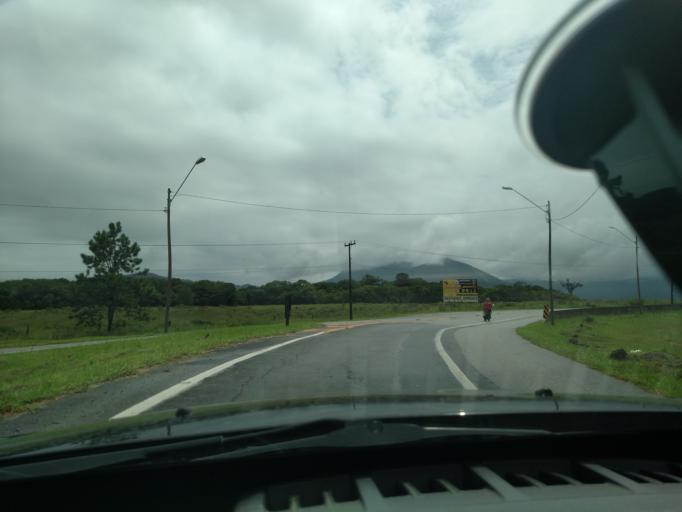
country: BR
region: Santa Catarina
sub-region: Porto Belo
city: Porto Belo
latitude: -27.1645
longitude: -48.6119
